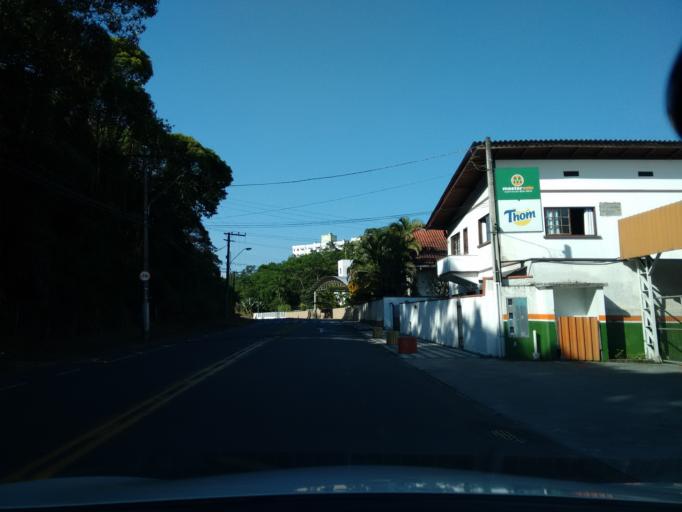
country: BR
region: Santa Catarina
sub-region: Blumenau
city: Blumenau
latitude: -26.8996
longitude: -49.0660
